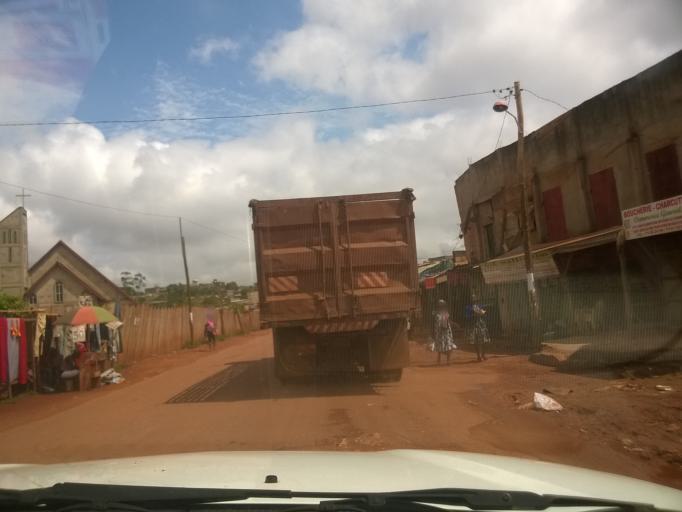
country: CM
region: Centre
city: Yaounde
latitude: 3.8707
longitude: 11.5430
